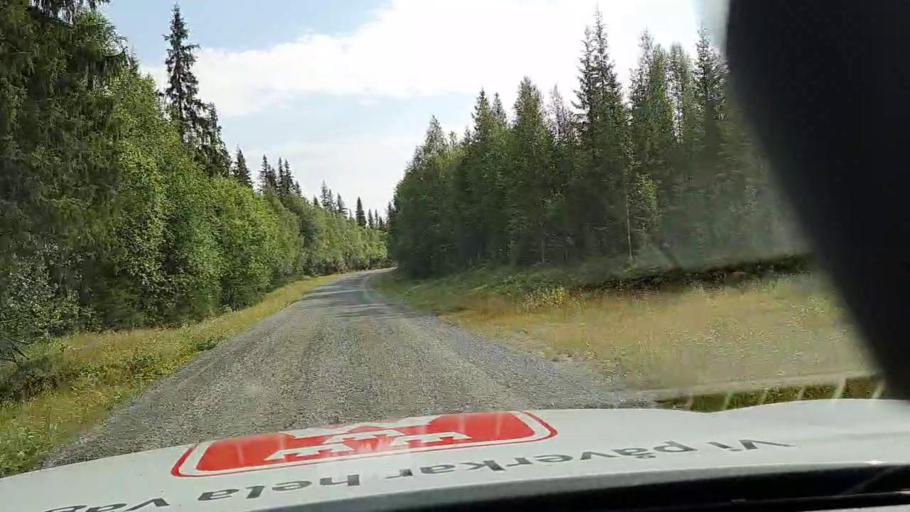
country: SE
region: Vaesterbotten
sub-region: Storumans Kommun
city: Fristad
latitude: 65.5389
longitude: 16.8048
